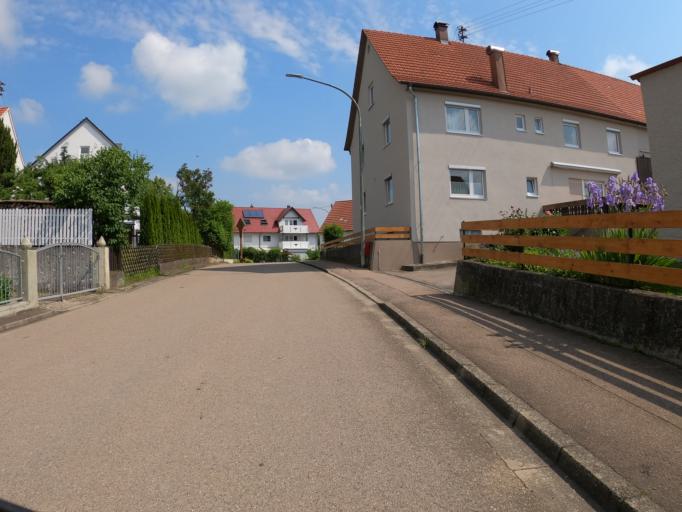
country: DE
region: Bavaria
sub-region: Swabia
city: Holzheim
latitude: 48.3772
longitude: 10.0938
